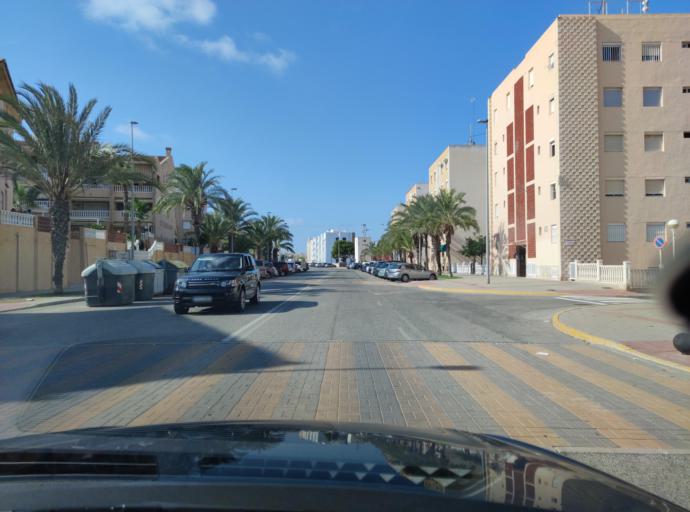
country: ES
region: Valencia
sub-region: Provincia de Alicante
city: Guardamar del Segura
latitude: 38.0766
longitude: -0.6502
